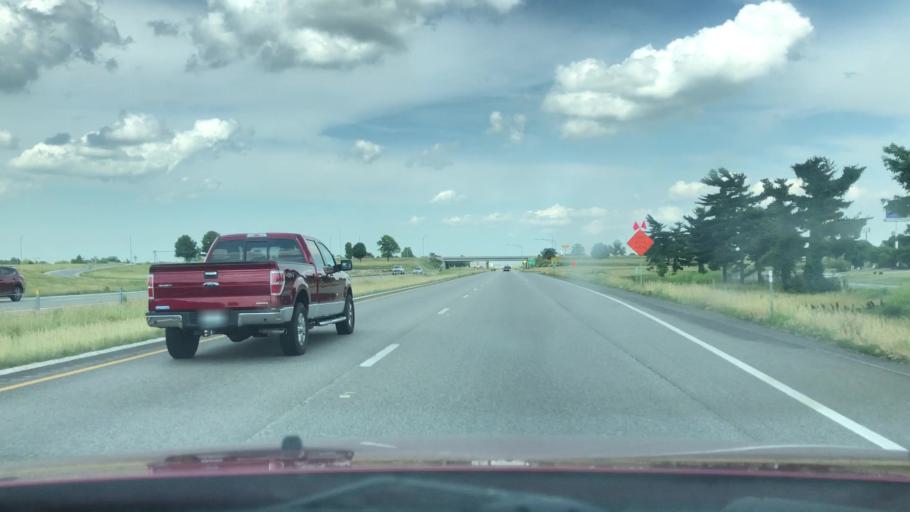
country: US
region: Missouri
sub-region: Greene County
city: Springfield
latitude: 37.2501
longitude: -93.2681
